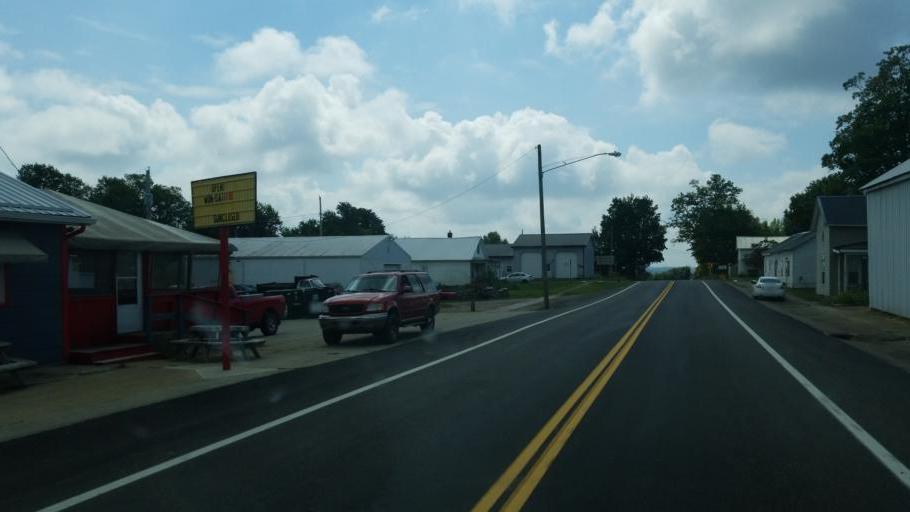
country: US
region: Ohio
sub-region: Licking County
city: Utica
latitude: 40.2694
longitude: -82.3541
